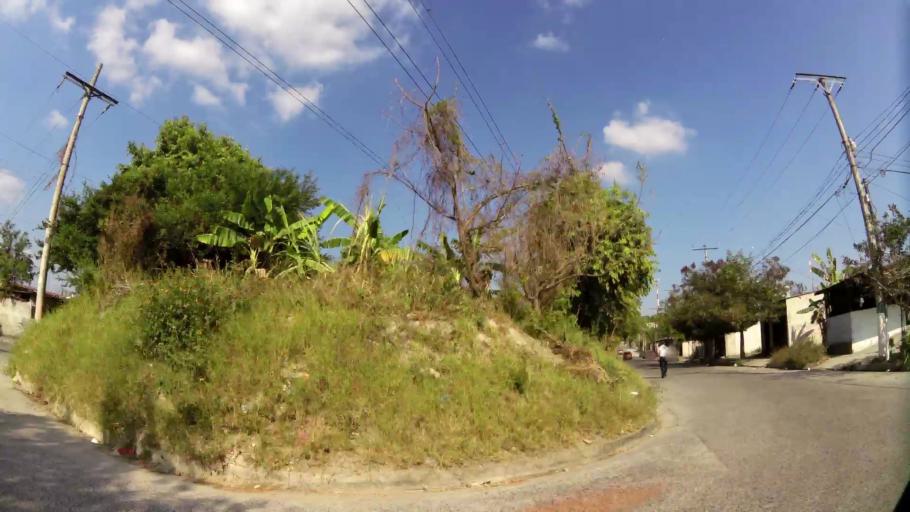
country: SV
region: San Salvador
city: Ilopango
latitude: 13.7257
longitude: -89.1109
